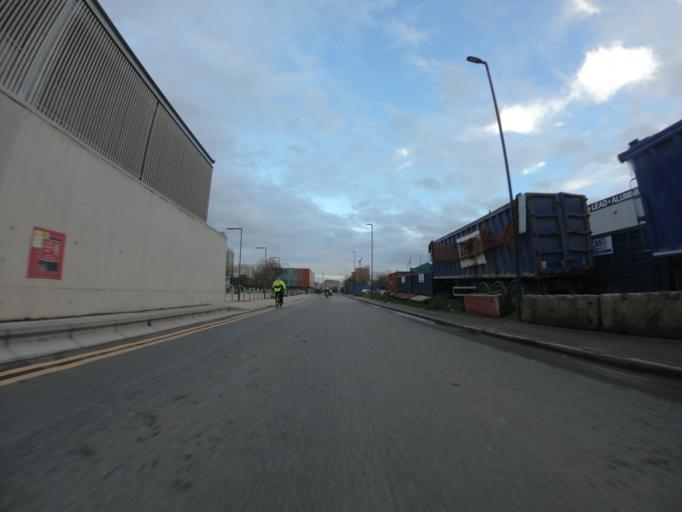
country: GB
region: England
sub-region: Greater London
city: Woolwich
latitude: 51.5007
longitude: 0.0560
